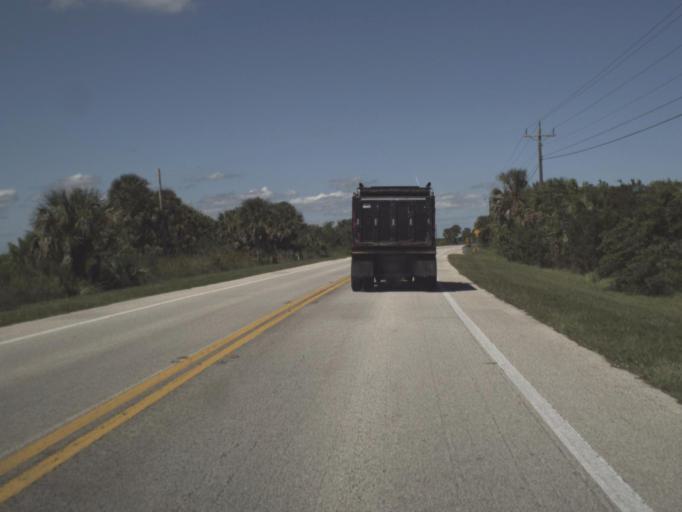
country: US
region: Florida
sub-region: Collier County
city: Marco
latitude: 25.9433
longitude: -81.4732
